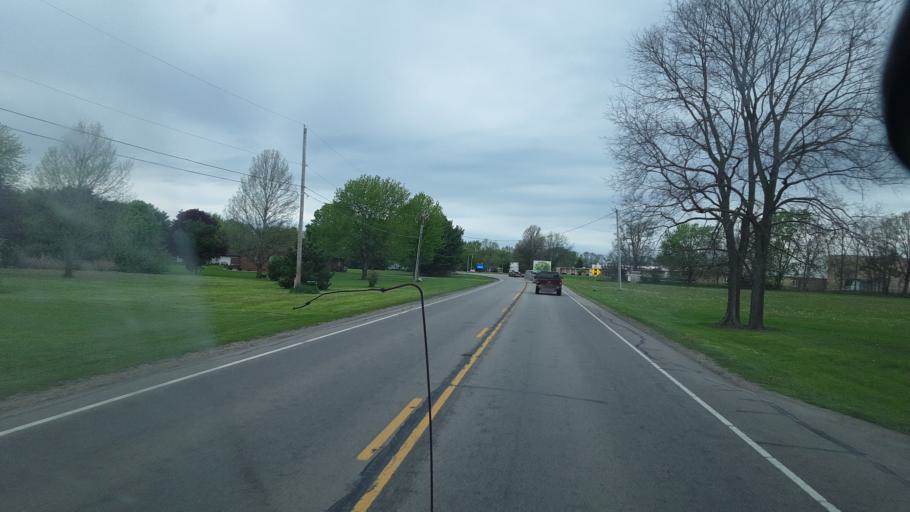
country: US
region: Indiana
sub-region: Elkhart County
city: New Paris
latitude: 41.5148
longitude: -85.7665
